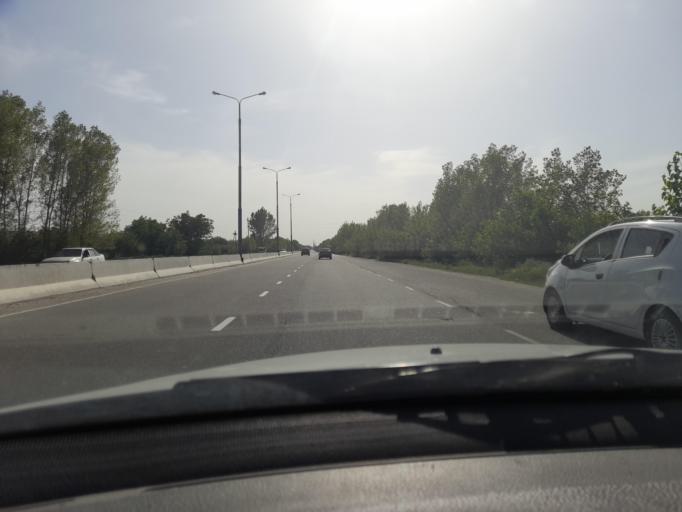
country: UZ
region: Samarqand
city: Ishtixon
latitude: 39.9513
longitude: 66.4322
